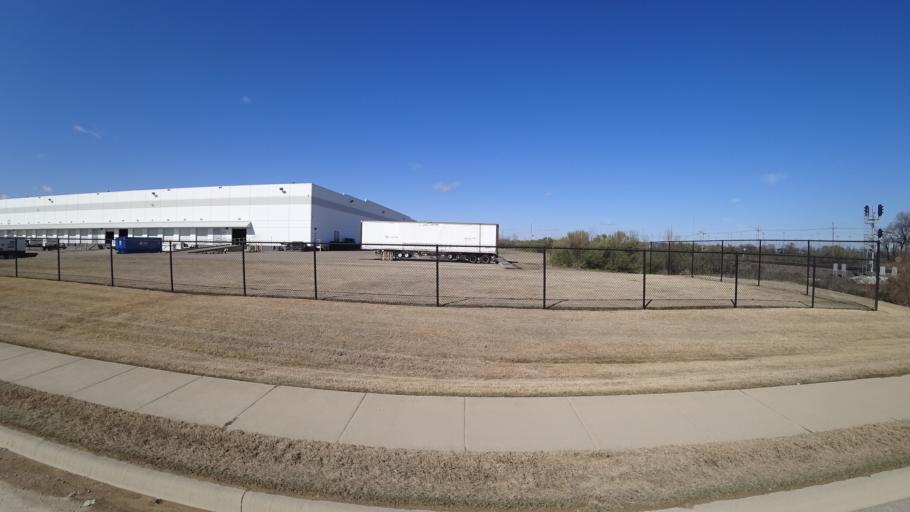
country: US
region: Texas
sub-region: Denton County
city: Lewisville
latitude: 33.0237
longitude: -96.9703
